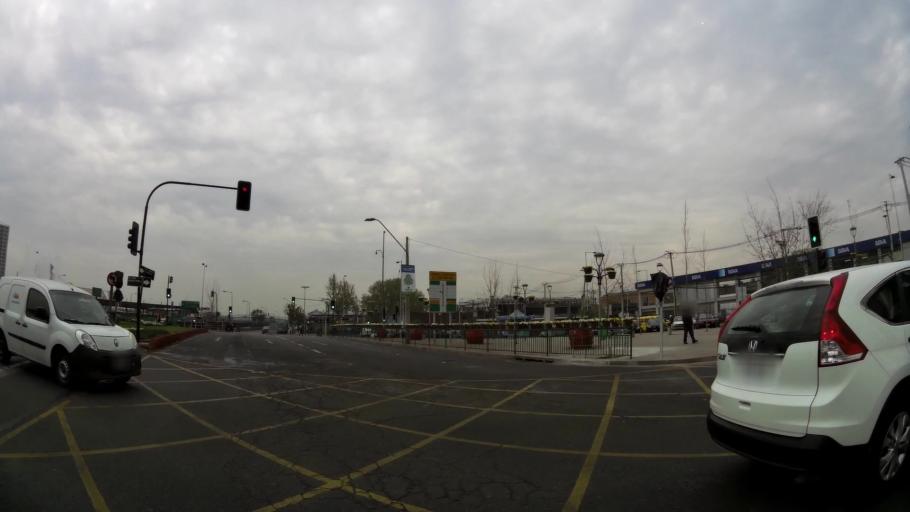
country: CL
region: Santiago Metropolitan
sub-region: Provincia de Santiago
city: Villa Presidente Frei, Nunoa, Santiago, Chile
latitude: -33.5222
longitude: -70.5987
